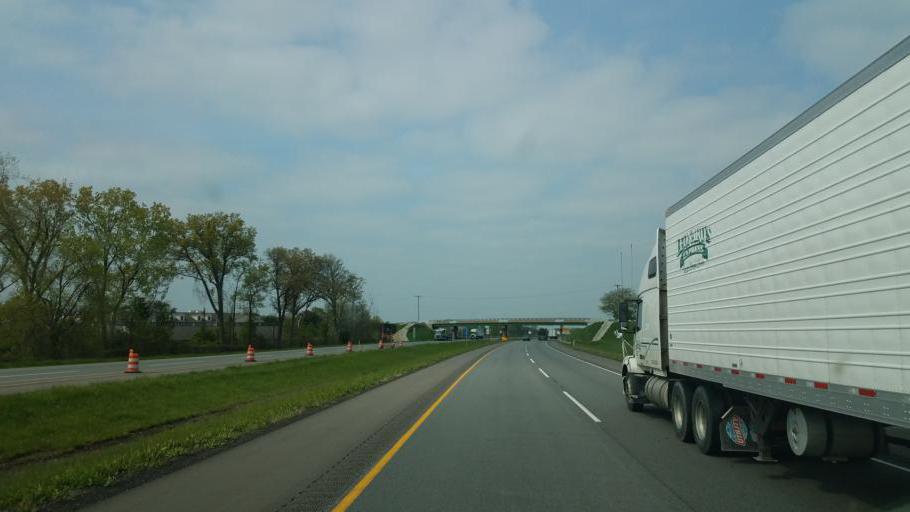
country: US
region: Indiana
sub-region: Saint Joseph County
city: Mishawaka
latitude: 41.7207
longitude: -86.1609
